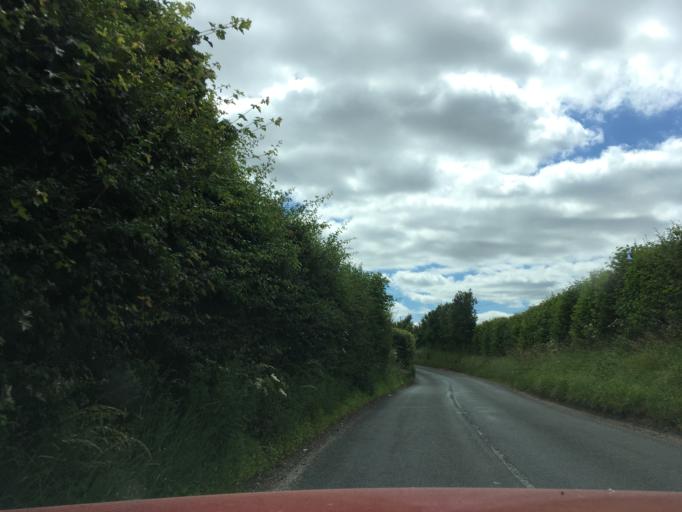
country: GB
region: England
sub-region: West Berkshire
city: Winterbourne
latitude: 51.4303
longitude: -1.3817
